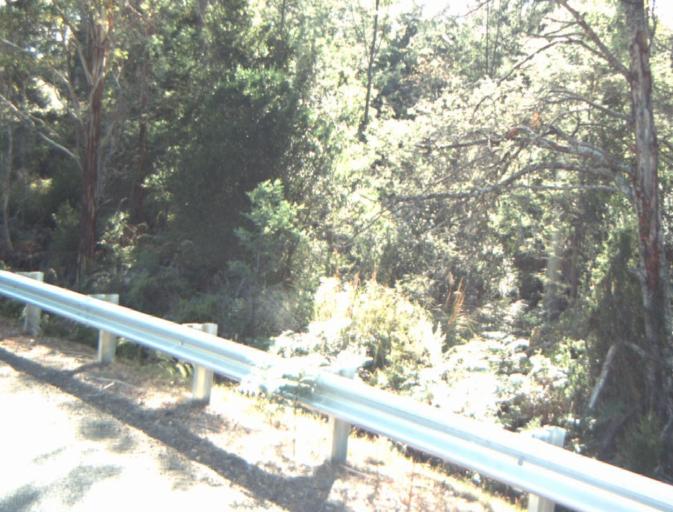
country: AU
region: Tasmania
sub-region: Launceston
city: Mayfield
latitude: -41.2921
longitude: 147.2056
